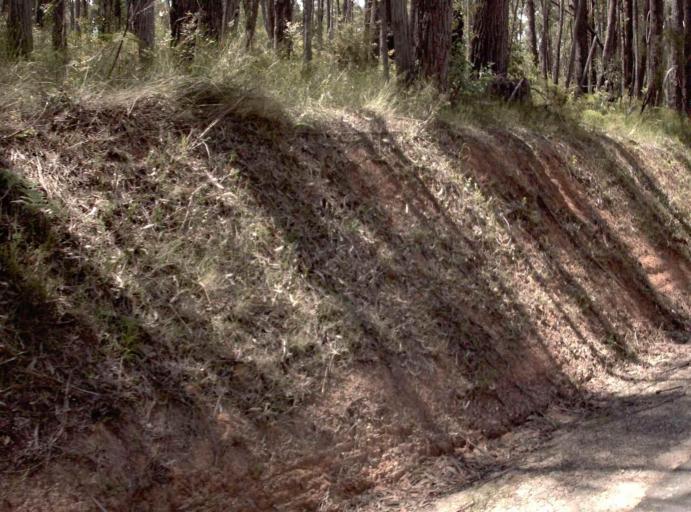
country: AU
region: New South Wales
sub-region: Bombala
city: Bombala
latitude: -37.5789
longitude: 149.0146
